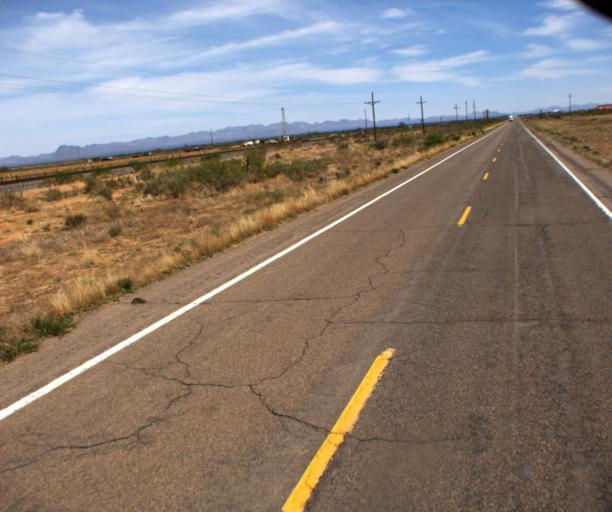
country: US
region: Arizona
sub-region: Cochise County
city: Willcox
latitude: 32.3226
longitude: -109.4625
